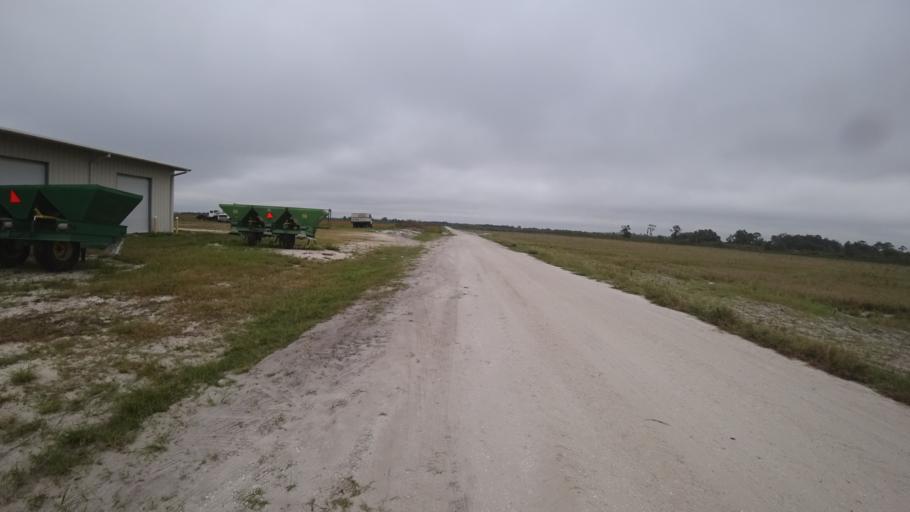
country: US
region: Florida
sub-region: Sarasota County
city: Warm Mineral Springs
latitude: 27.3012
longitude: -82.1441
